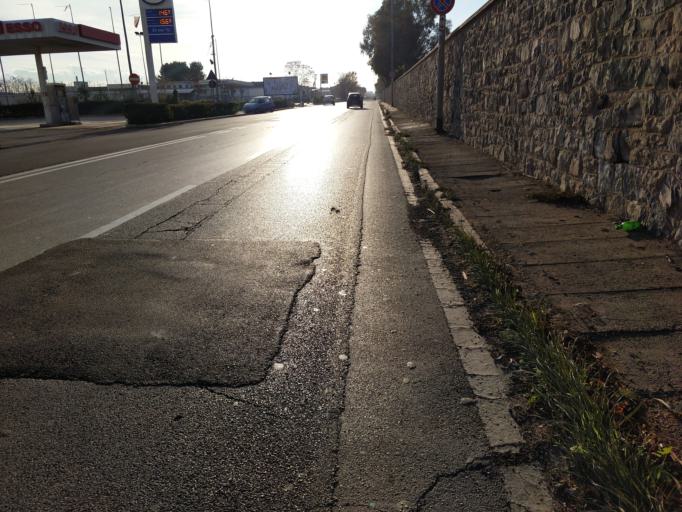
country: IT
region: Apulia
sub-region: Provincia di Bari
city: Bari
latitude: 41.1148
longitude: 16.8339
